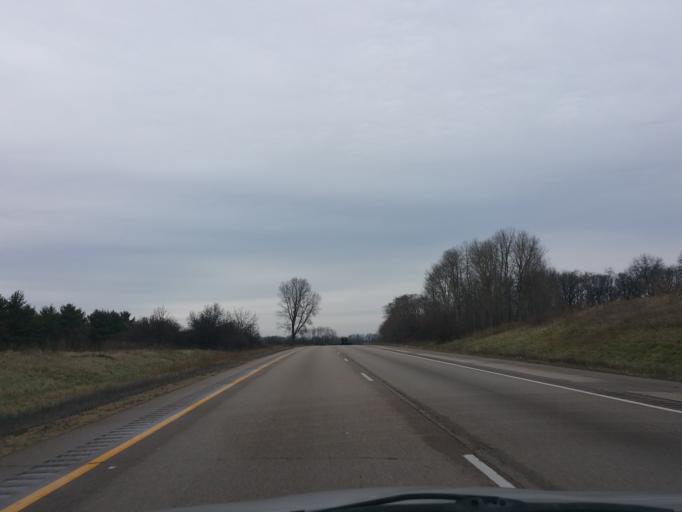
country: US
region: Wisconsin
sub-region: Jefferson County
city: Cambridge
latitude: 42.9489
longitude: -89.0960
